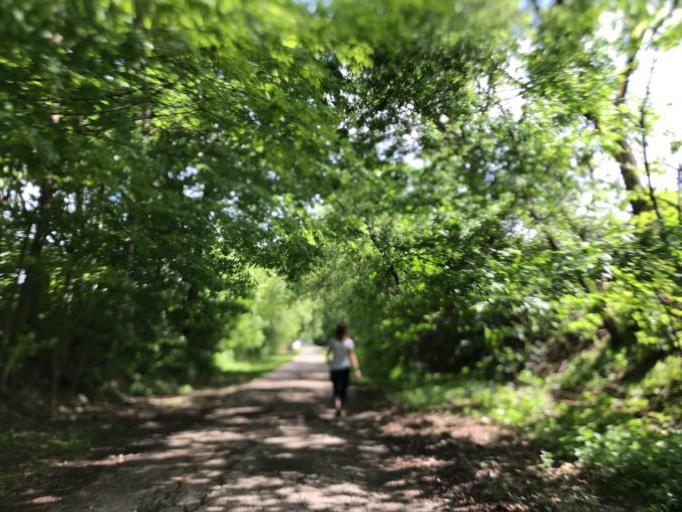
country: US
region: Michigan
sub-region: Oakland County
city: South Lyon
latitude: 42.4630
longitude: -83.6466
